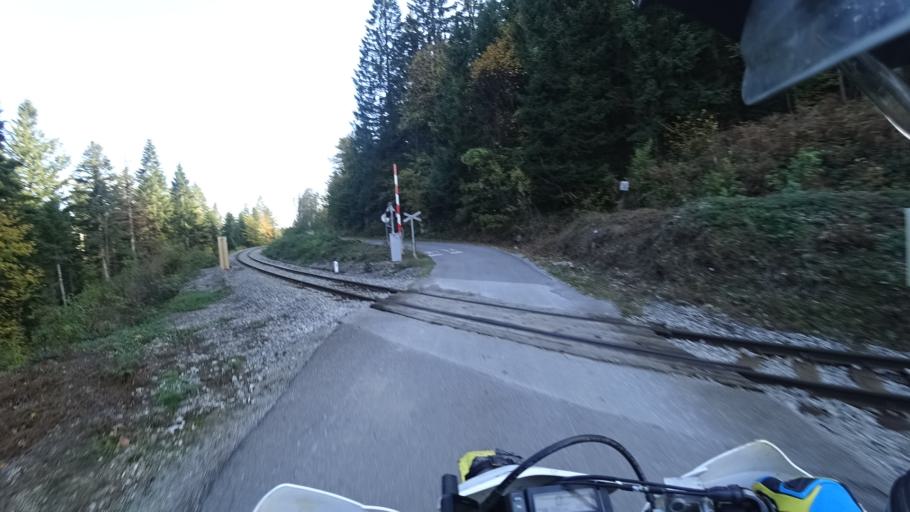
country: HR
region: Karlovacka
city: Plaski
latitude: 44.9935
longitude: 15.4164
